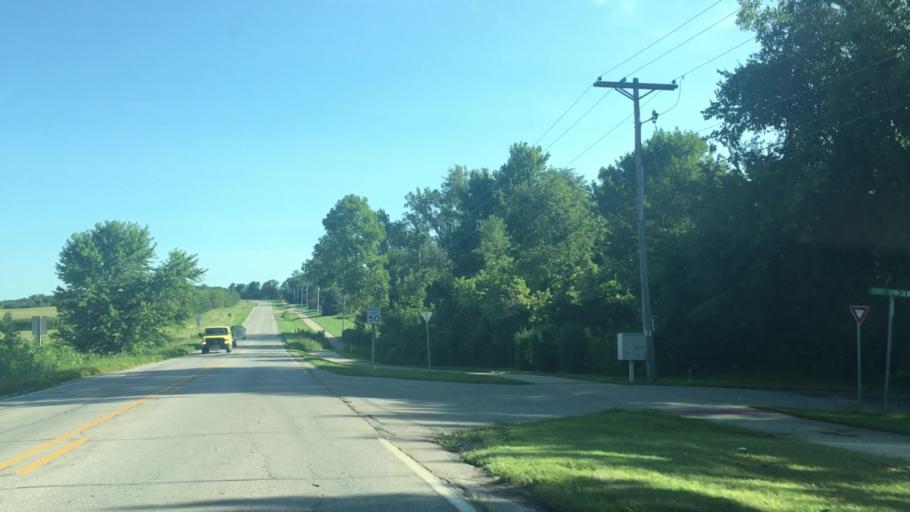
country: US
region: Iowa
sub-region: Johnson County
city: North Liberty
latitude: 41.7239
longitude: -91.5610
